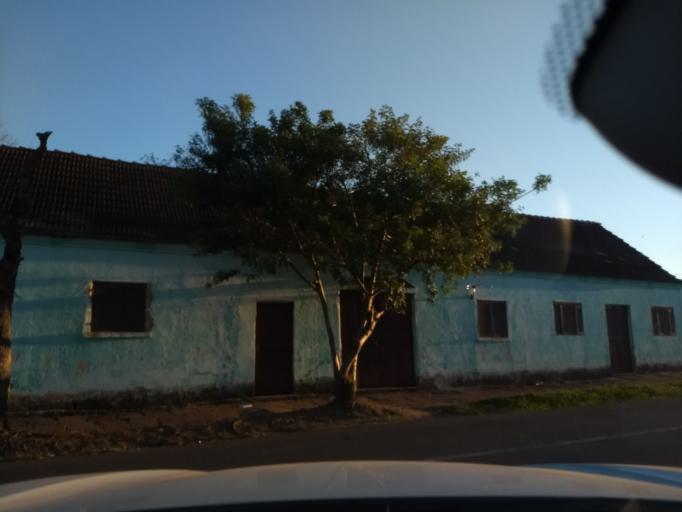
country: BR
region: Rio Grande do Sul
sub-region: Santa Cruz Do Sul
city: Santa Cruz do Sul
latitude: -29.7202
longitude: -52.5222
